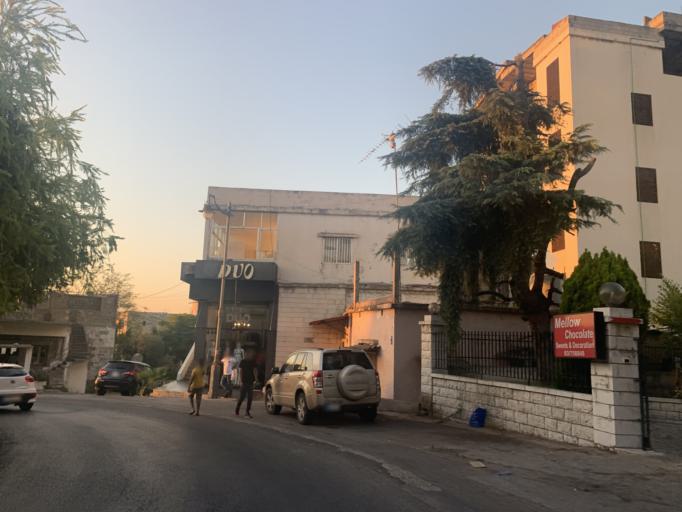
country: LB
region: Mont-Liban
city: Djounie
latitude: 33.9661
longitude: 35.6264
